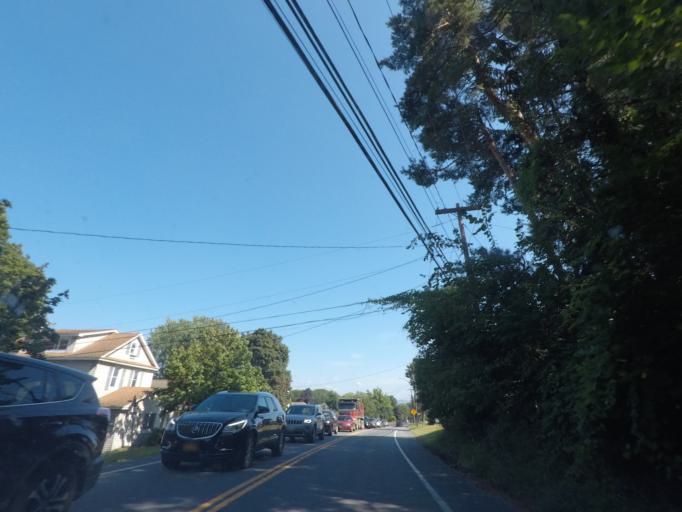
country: US
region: New York
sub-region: Albany County
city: Menands
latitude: 42.7361
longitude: -73.7594
